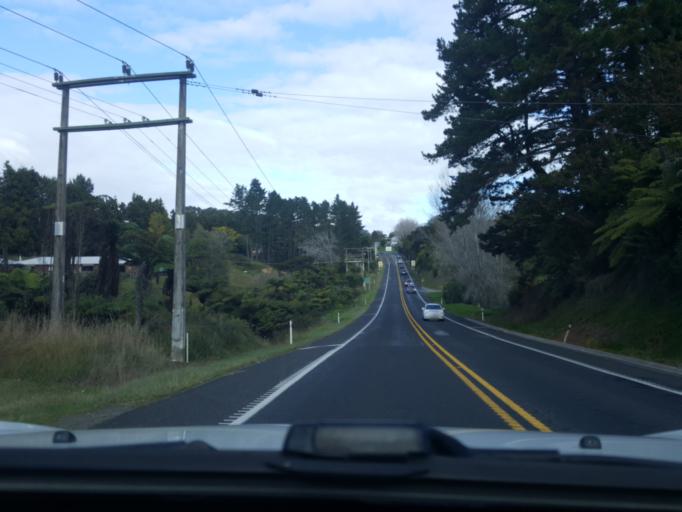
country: NZ
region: Bay of Plenty
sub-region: Western Bay of Plenty District
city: Katikati
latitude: -37.6490
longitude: 175.9948
